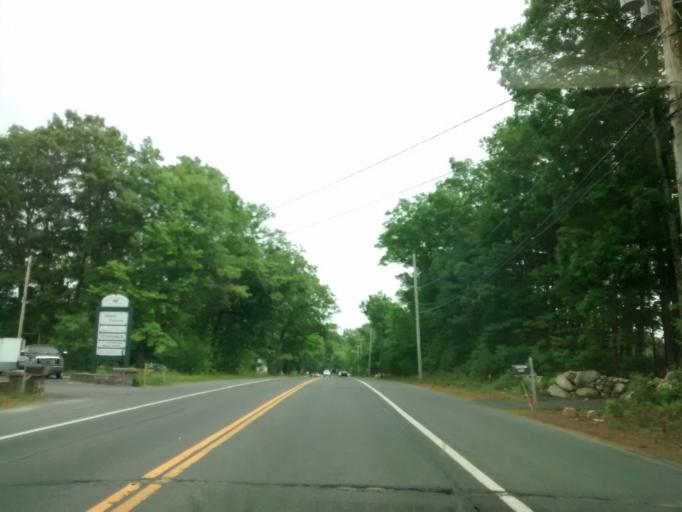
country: US
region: Massachusetts
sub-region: Worcester County
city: Millville
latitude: 42.0122
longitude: -71.5921
